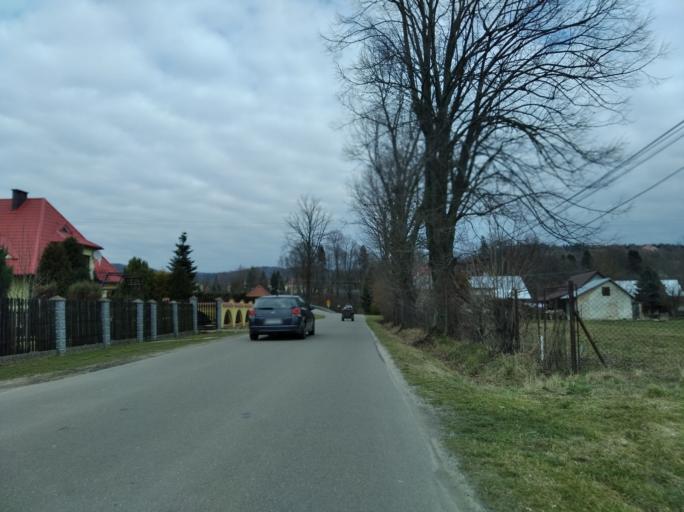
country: PL
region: Subcarpathian Voivodeship
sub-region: Powiat strzyzowski
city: Frysztak
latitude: 49.8367
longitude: 21.6184
